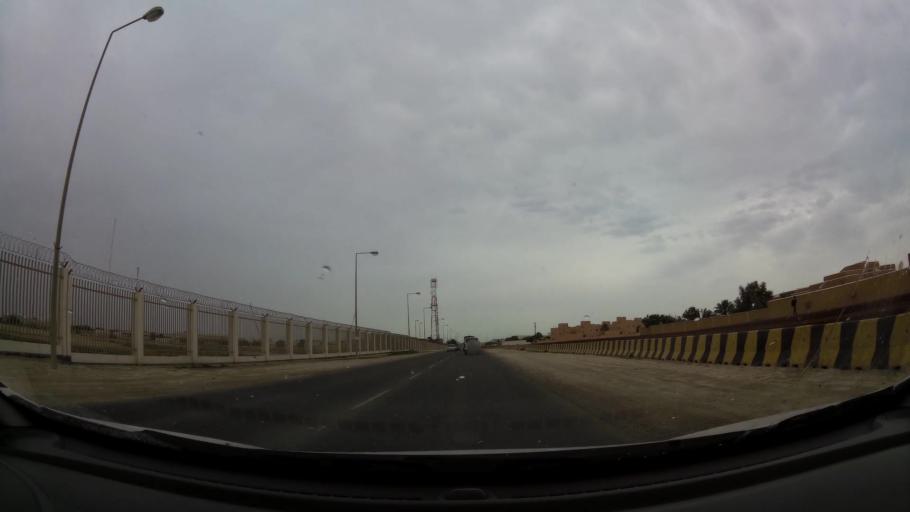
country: BH
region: Central Governorate
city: Madinat Hamad
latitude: 26.1593
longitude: 50.4763
